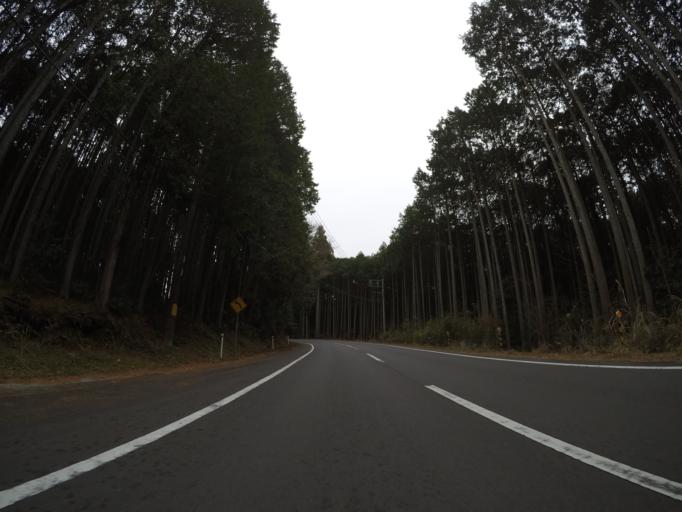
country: JP
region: Shizuoka
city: Fujinomiya
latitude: 35.2392
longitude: 138.5734
